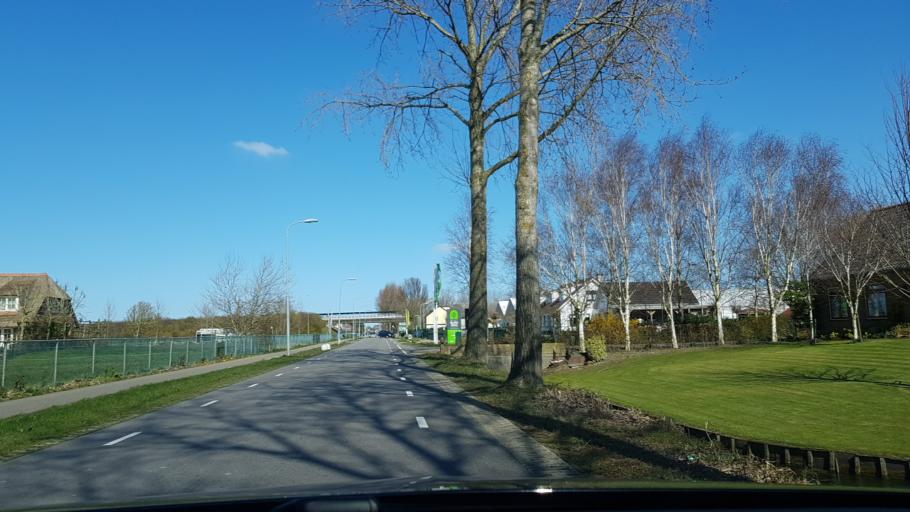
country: NL
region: North Holland
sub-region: Gemeente Bloemendaal
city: Bennebroek
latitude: 52.2943
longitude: 4.6367
